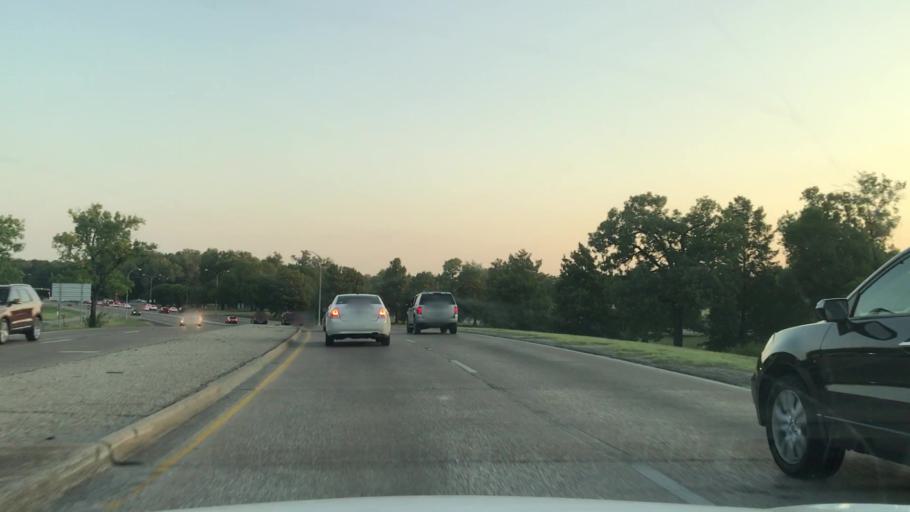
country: US
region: Texas
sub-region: Dallas County
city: Highland Park
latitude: 32.8573
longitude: -96.7176
